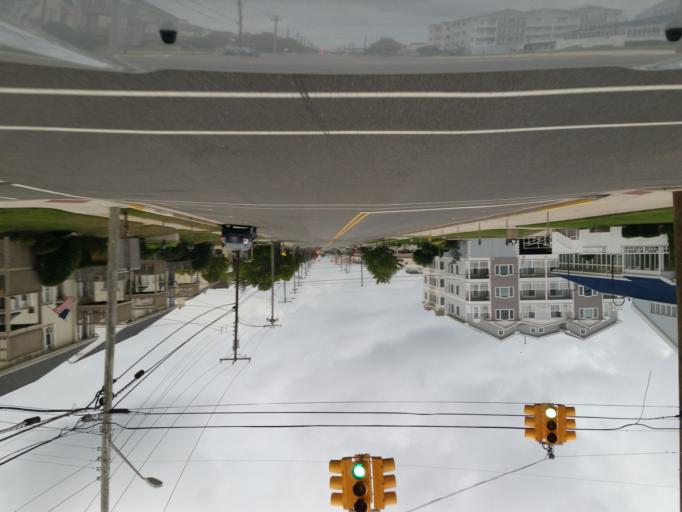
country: US
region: New Jersey
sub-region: Cape May County
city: Wildwood Crest
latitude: 38.9771
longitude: -74.8272
